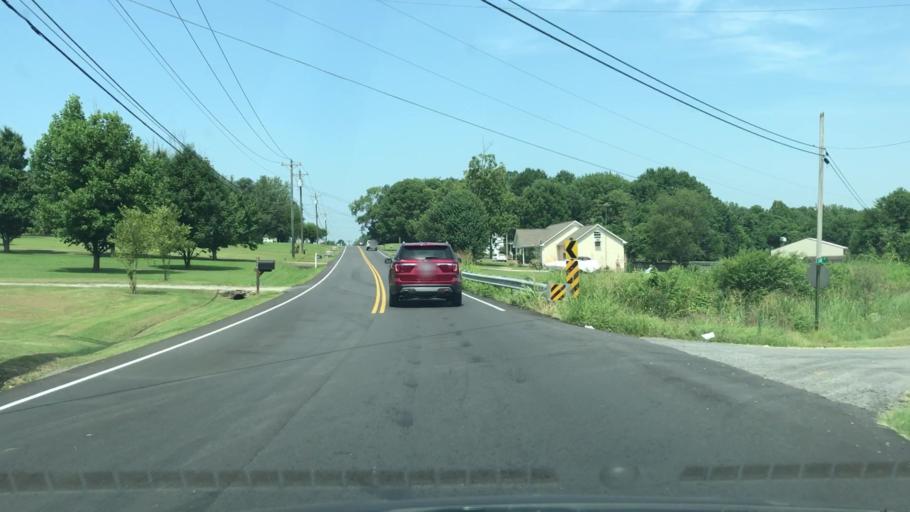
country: US
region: Tennessee
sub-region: Wilson County
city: Rural Hill
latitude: 36.1219
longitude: -86.5028
